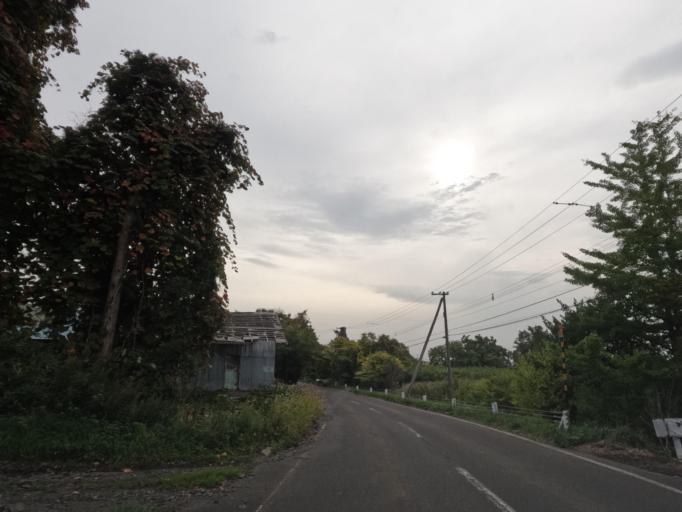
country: JP
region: Hokkaido
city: Date
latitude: 42.4621
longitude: 140.9046
